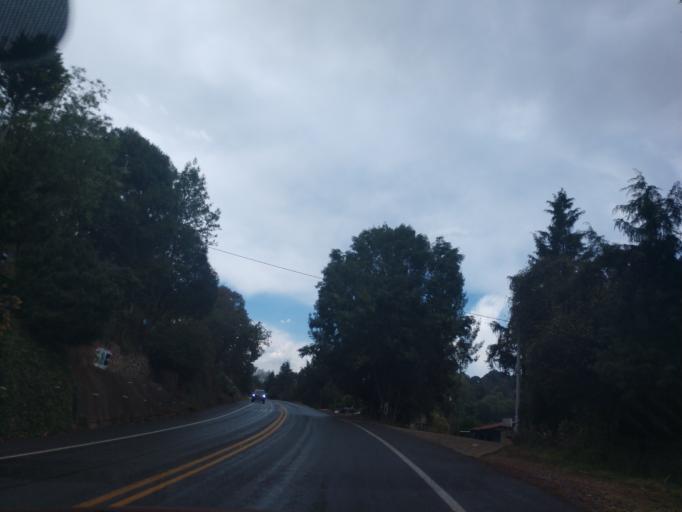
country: MX
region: Jalisco
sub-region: Mazamitla
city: Mazamitla
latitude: 19.9432
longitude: -103.0643
